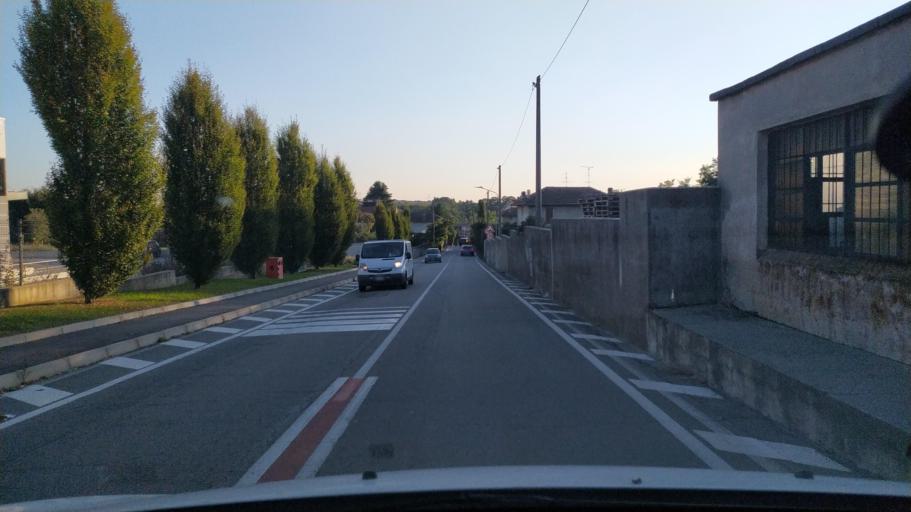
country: IT
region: Lombardy
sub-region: Provincia di Varese
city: Sesto Calende
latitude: 45.7272
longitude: 8.6474
